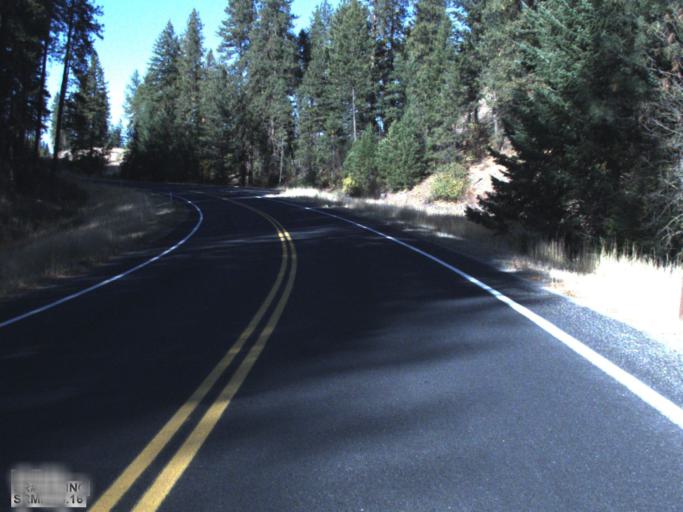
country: US
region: Washington
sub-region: Lincoln County
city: Davenport
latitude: 48.0506
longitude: -118.2214
